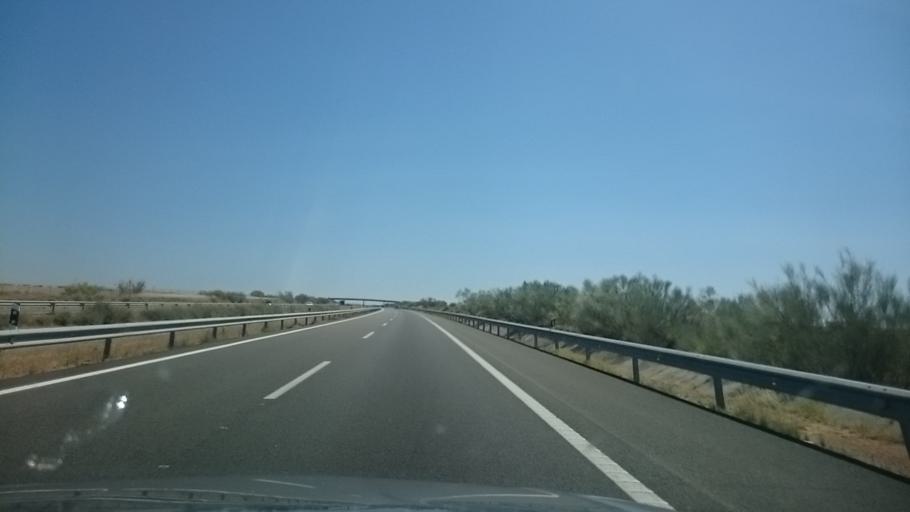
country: ES
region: Aragon
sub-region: Provincia de Zaragoza
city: Mequinensa / Mequinenza
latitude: 41.4675
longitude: 0.2447
